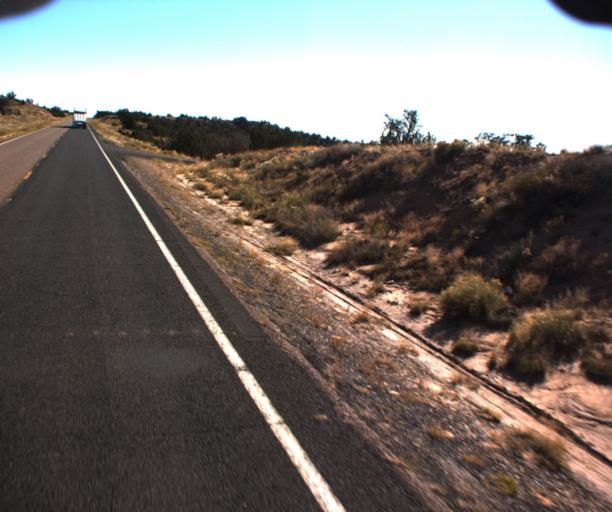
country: US
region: Arizona
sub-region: Apache County
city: Ganado
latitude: 35.4538
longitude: -109.5220
